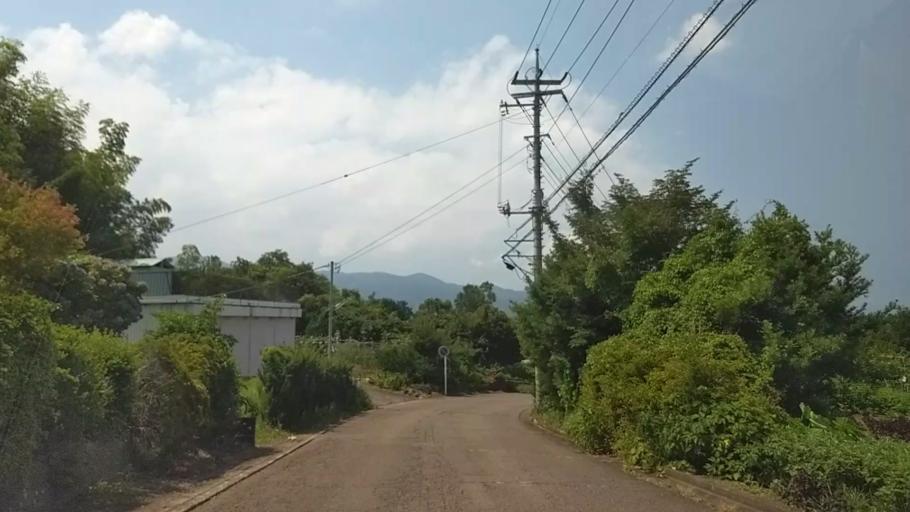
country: JP
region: Shizuoka
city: Ito
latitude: 34.9453
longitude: 139.1054
